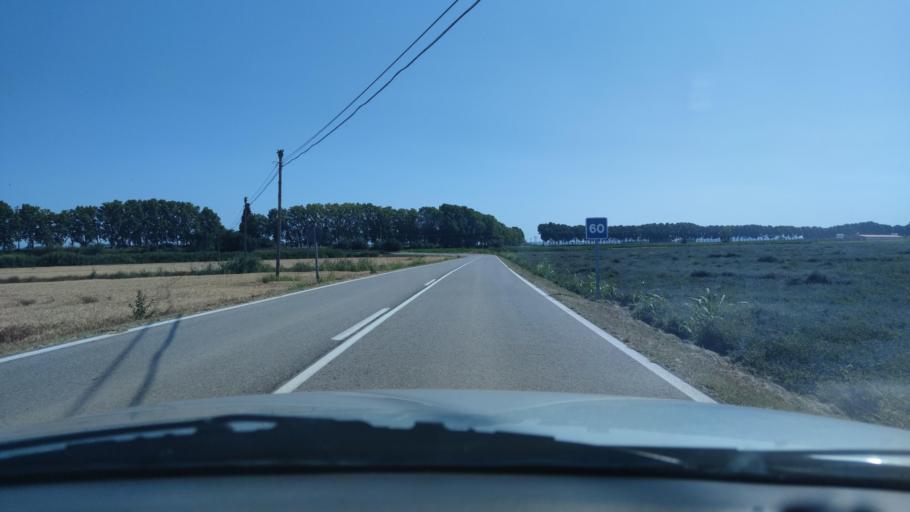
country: ES
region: Catalonia
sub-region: Provincia de Lleida
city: Bellcaire d'Urgell
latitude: 41.7265
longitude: 0.9240
